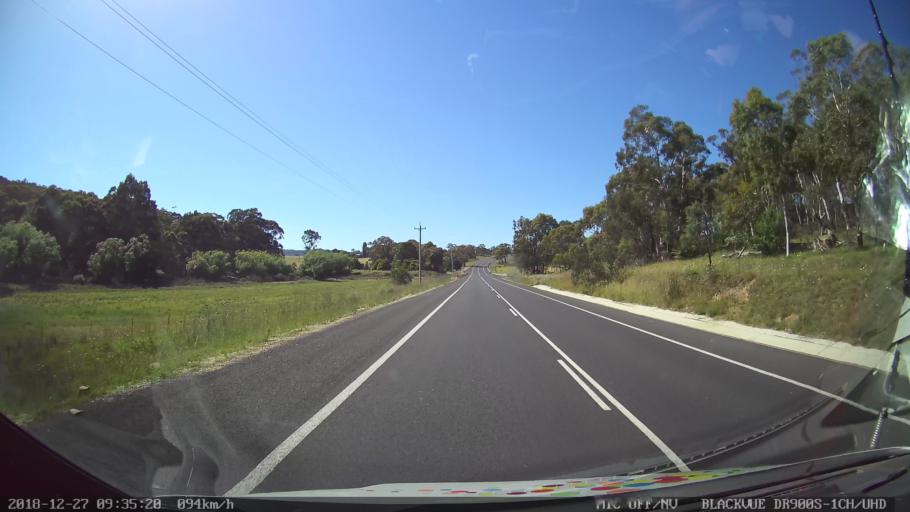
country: AU
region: New South Wales
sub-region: Lithgow
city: Portland
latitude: -33.2373
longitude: 150.0297
